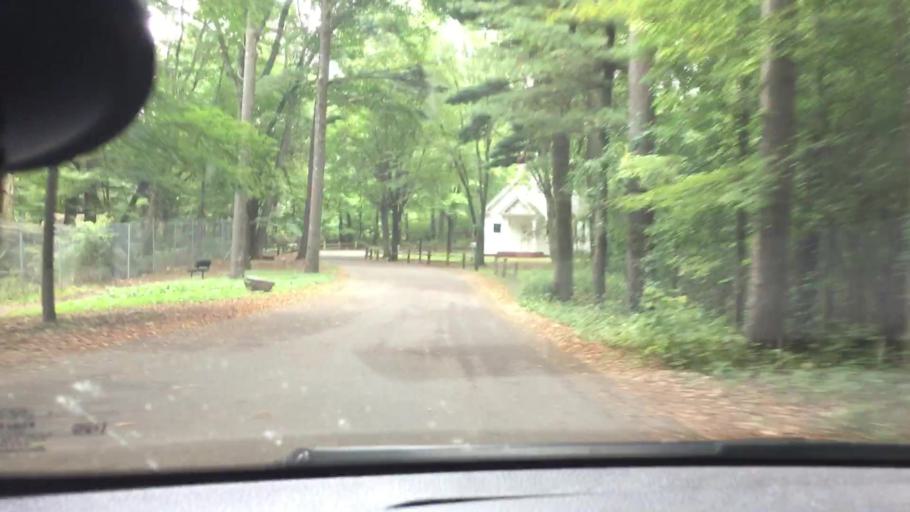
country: US
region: Wisconsin
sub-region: Chippewa County
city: Chippewa Falls
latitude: 44.9537
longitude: -91.4025
